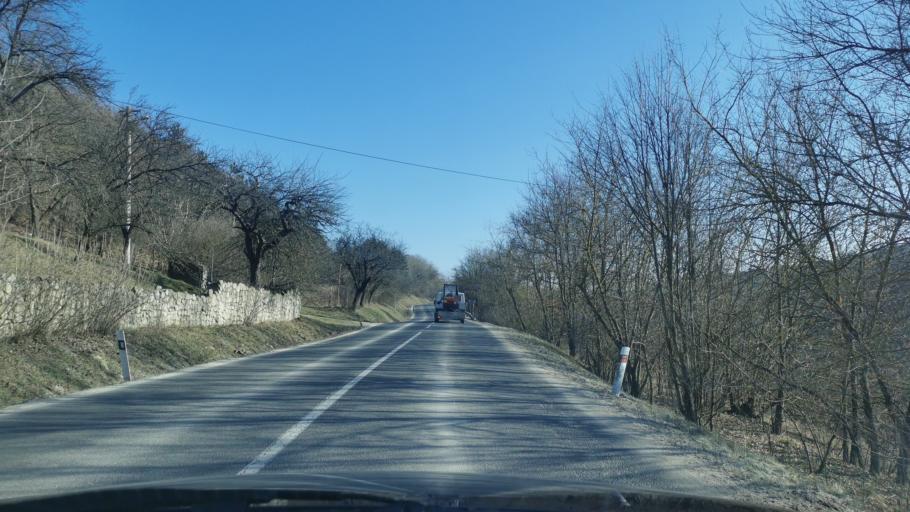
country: SK
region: Trenciansky
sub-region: Okres Myjava
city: Myjava
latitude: 48.7522
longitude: 17.5007
